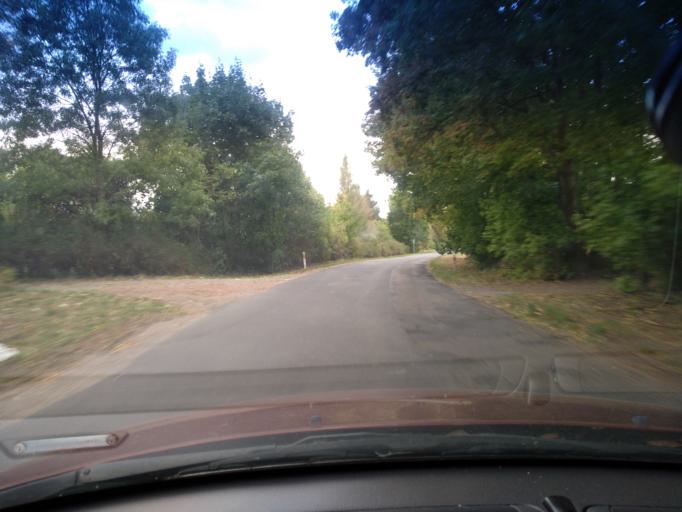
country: PL
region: Lower Silesian Voivodeship
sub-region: Powiat zgorzelecki
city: Zgorzelec
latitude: 51.1708
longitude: 15.0079
